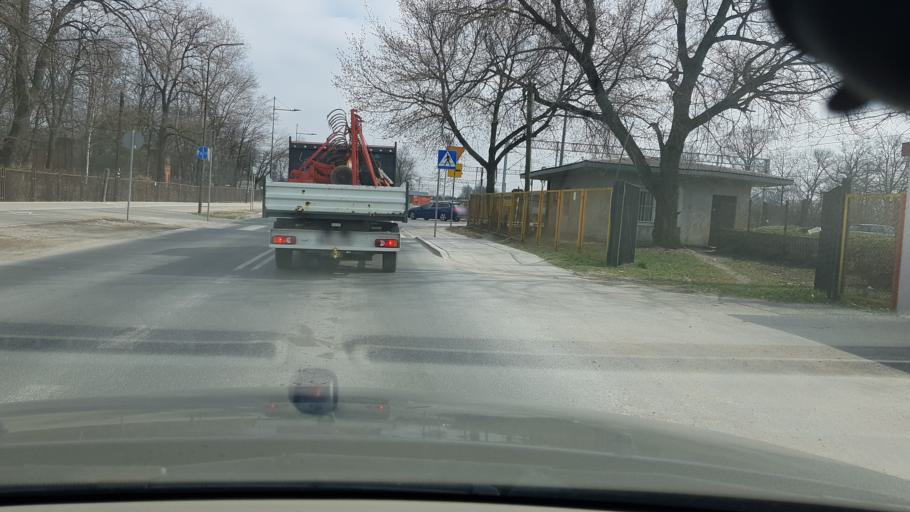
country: PL
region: Masovian Voivodeship
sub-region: Warszawa
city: Rembertow
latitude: 52.2575
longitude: 21.1557
